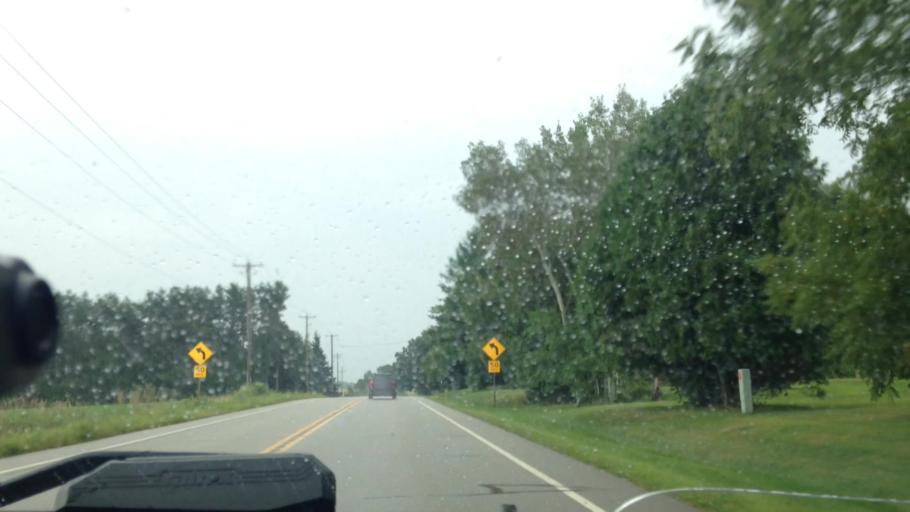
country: US
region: Wisconsin
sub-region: Washington County
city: Hartford
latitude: 43.3934
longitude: -88.3607
